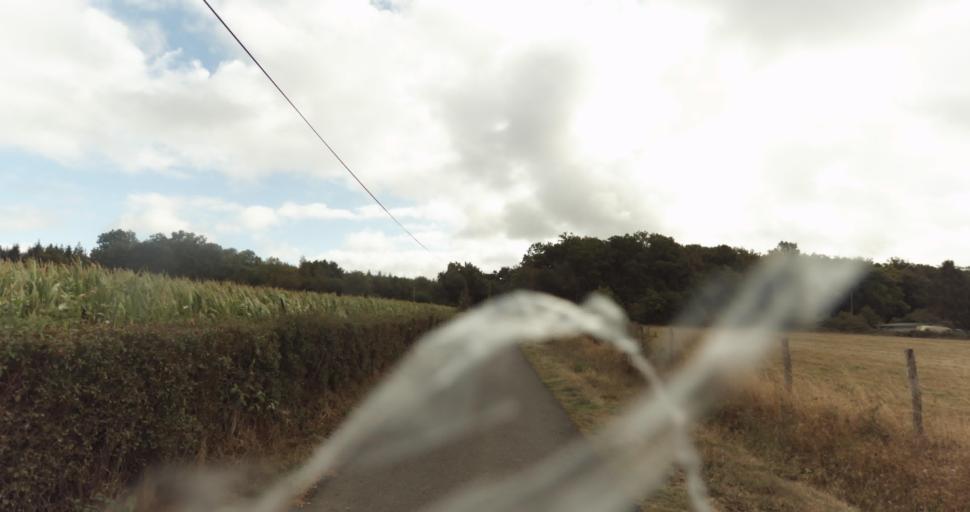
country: FR
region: Lower Normandy
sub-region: Departement de l'Orne
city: Gace
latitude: 48.8481
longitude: 0.3206
